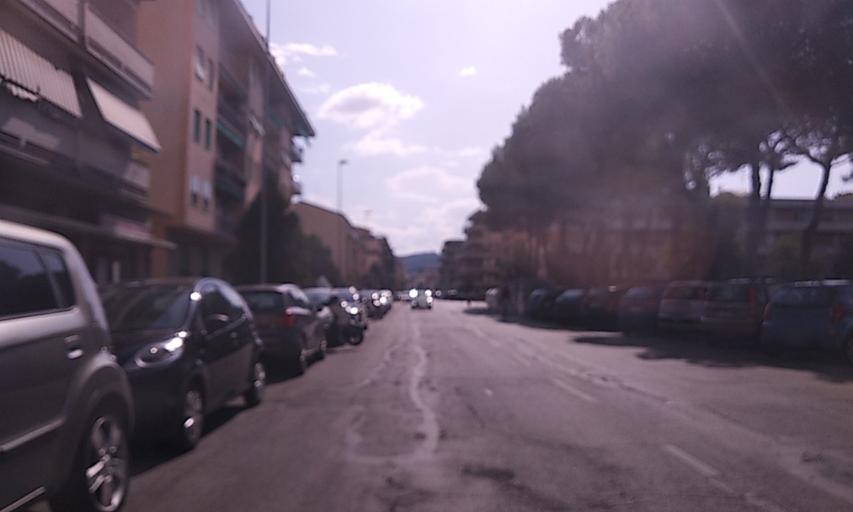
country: IT
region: Tuscany
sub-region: Province of Florence
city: Scandicci
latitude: 43.7561
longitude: 11.1867
